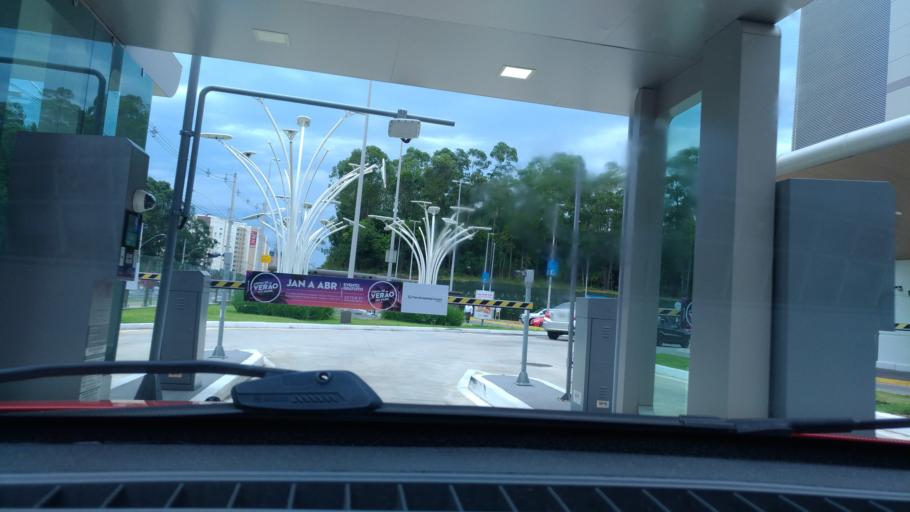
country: BR
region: Rio Grande do Sul
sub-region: Canoas
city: Canoas
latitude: -29.9150
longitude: -51.1655
